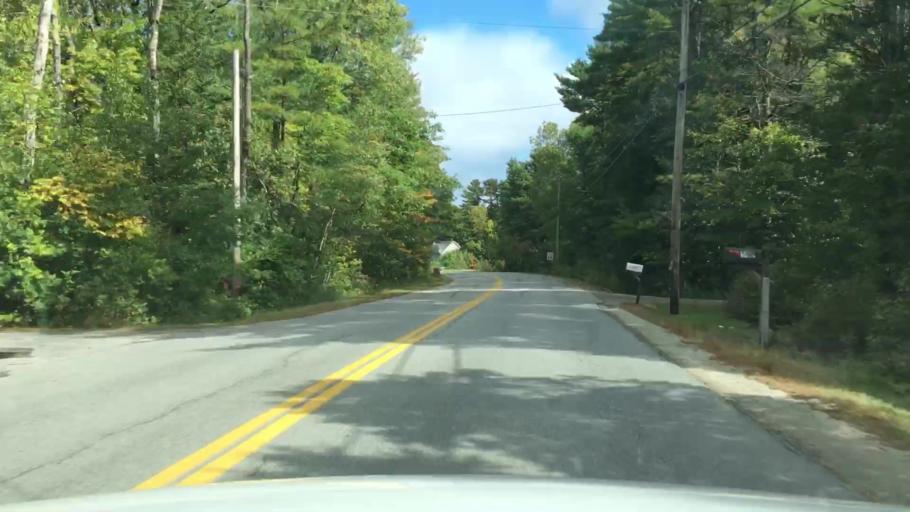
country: US
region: Maine
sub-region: Cumberland County
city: Brunswick
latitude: 43.9319
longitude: -69.9089
